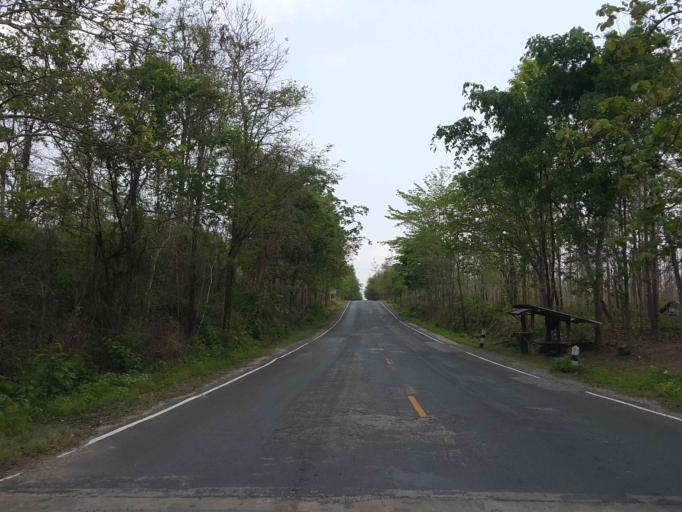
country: TH
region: Sukhothai
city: Thung Saliam
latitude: 17.4087
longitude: 99.3890
